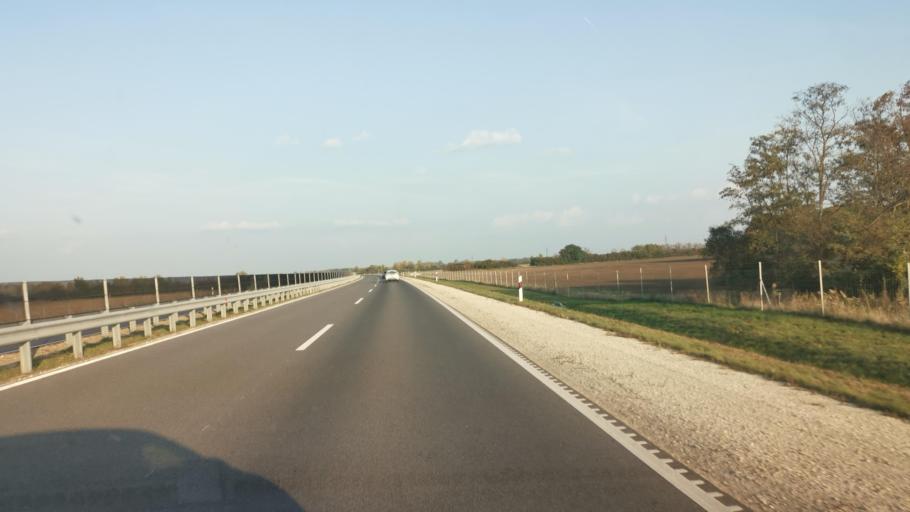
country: HU
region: Gyor-Moson-Sopron
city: Mihalyi
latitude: 47.5647
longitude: 17.1191
